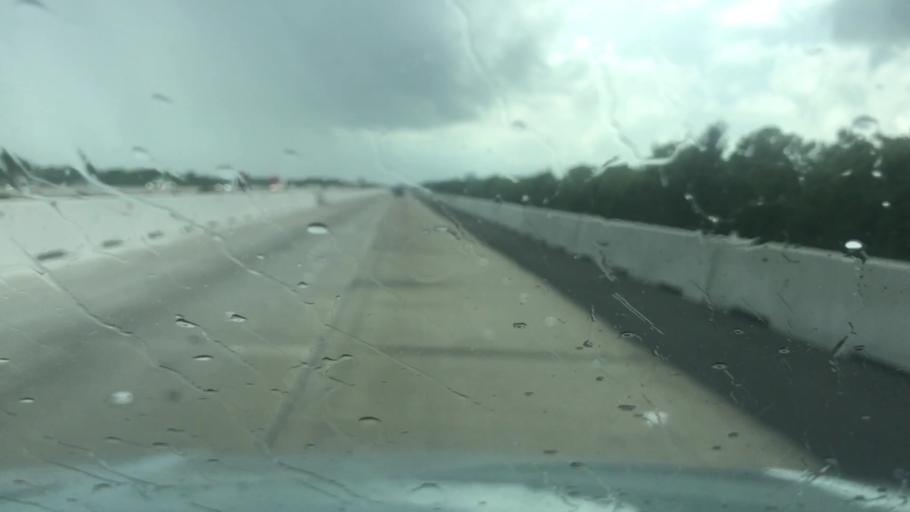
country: US
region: Texas
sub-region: Waller County
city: Brookshire
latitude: 29.7802
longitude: -95.9996
